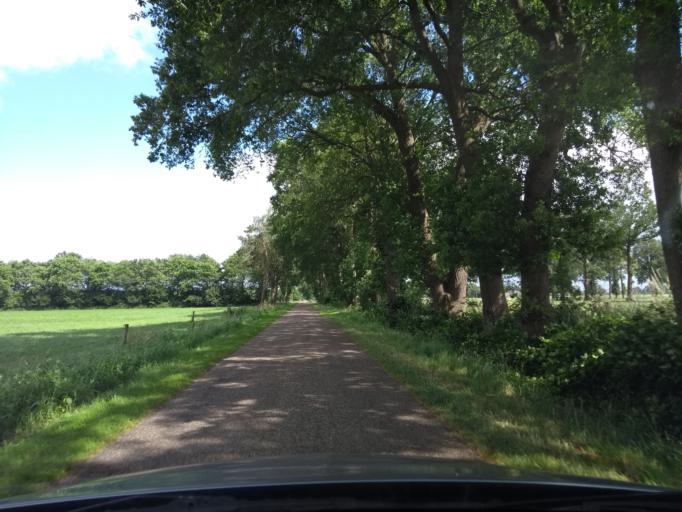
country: NL
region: Overijssel
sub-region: Gemeente Twenterand
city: Den Ham
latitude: 52.4279
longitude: 6.4863
